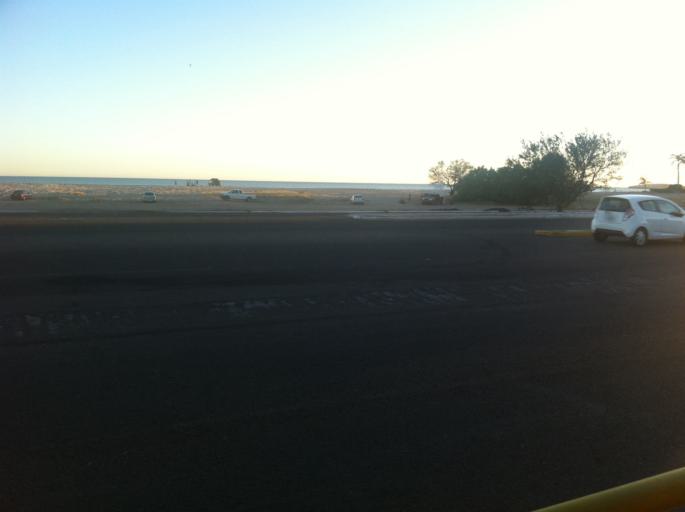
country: MX
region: Sonora
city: Heroica Guaymas
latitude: 27.9652
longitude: -111.0178
